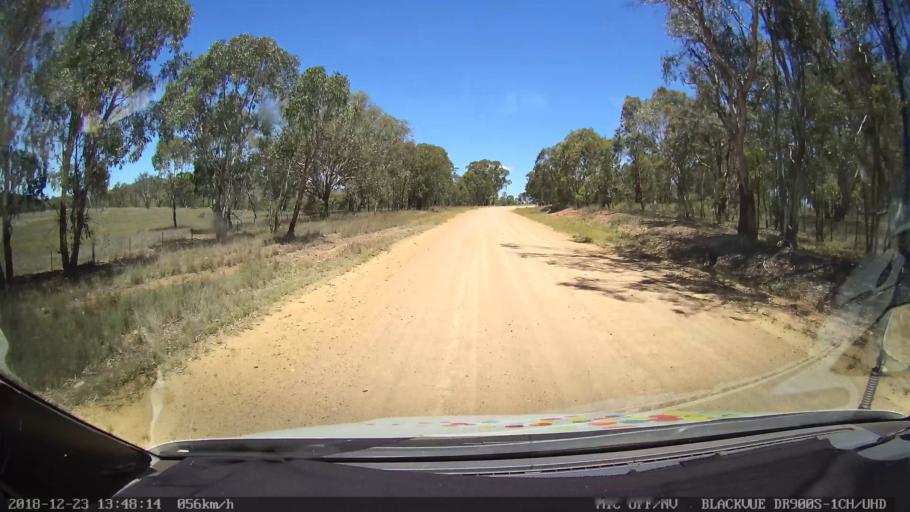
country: AU
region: New South Wales
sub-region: Tamworth Municipality
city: Manilla
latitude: -30.5158
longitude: 151.1164
